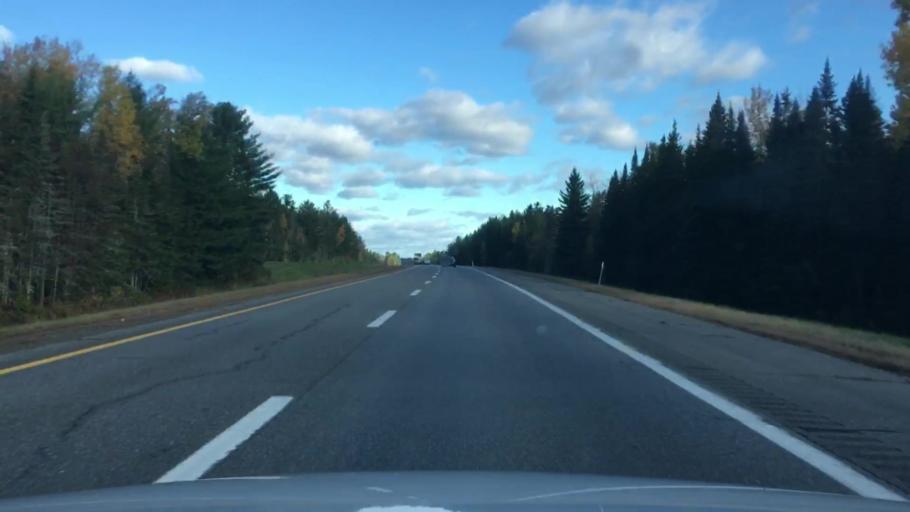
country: US
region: Maine
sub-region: Penobscot County
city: Greenbush
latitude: 45.1238
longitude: -68.6945
